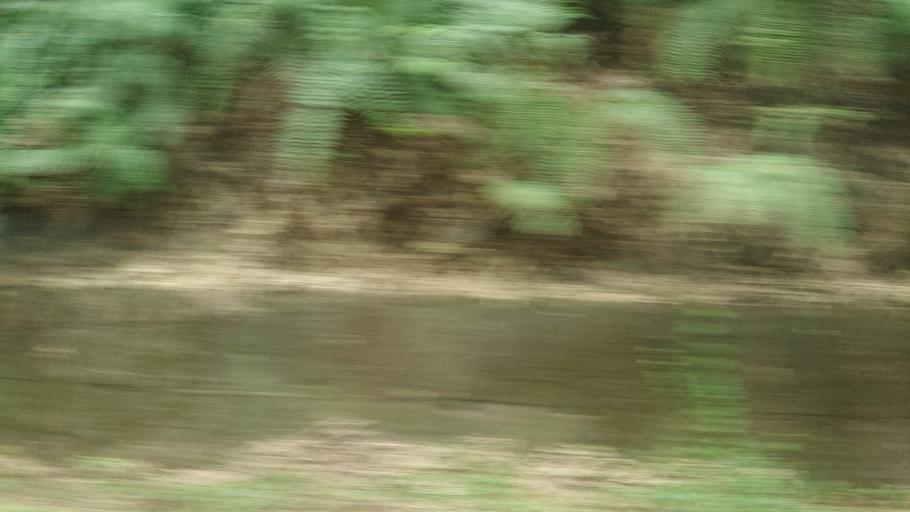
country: TW
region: Taiwan
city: Lugu
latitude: 23.6289
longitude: 120.7156
